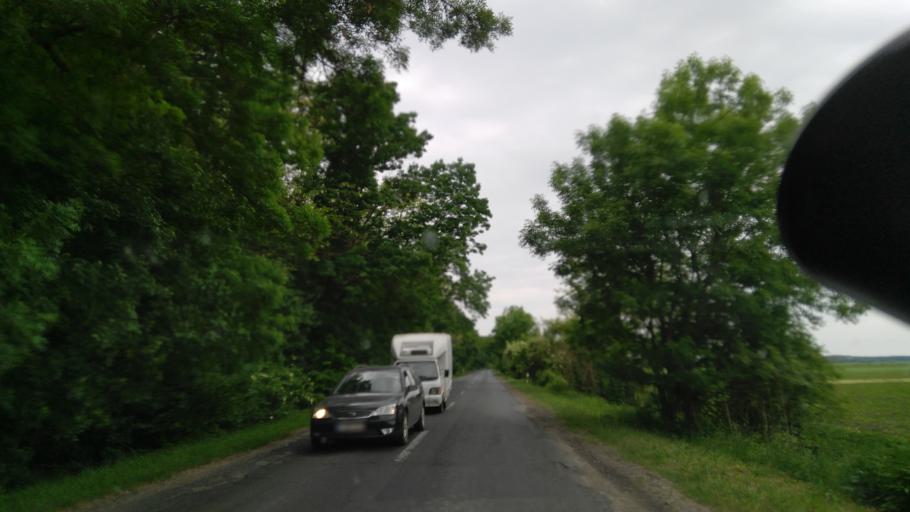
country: HU
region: Bekes
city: Doboz
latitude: 46.7301
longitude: 21.2714
